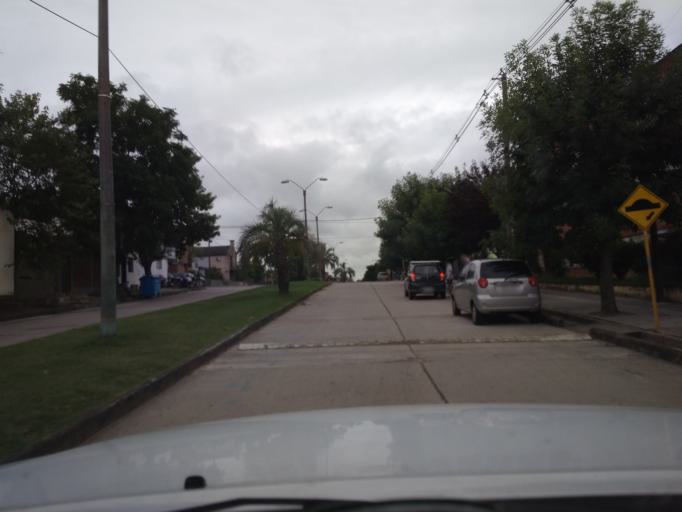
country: UY
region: Florida
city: Florida
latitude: -34.1031
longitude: -56.2076
